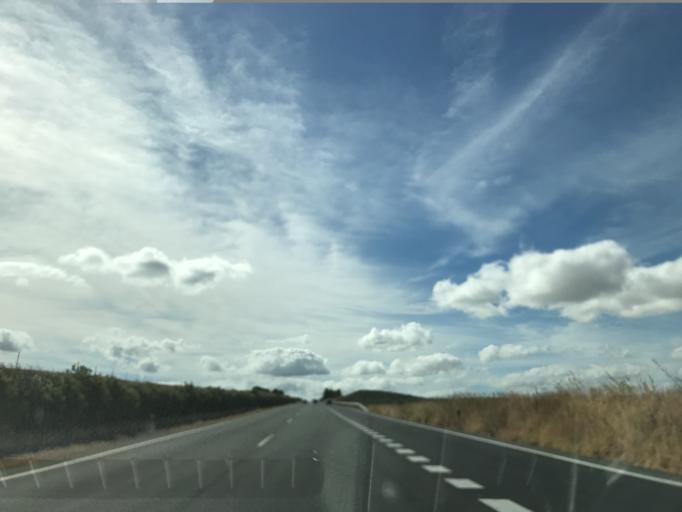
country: ES
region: Andalusia
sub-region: Province of Cordoba
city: La Victoria
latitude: 37.7287
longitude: -4.8556
